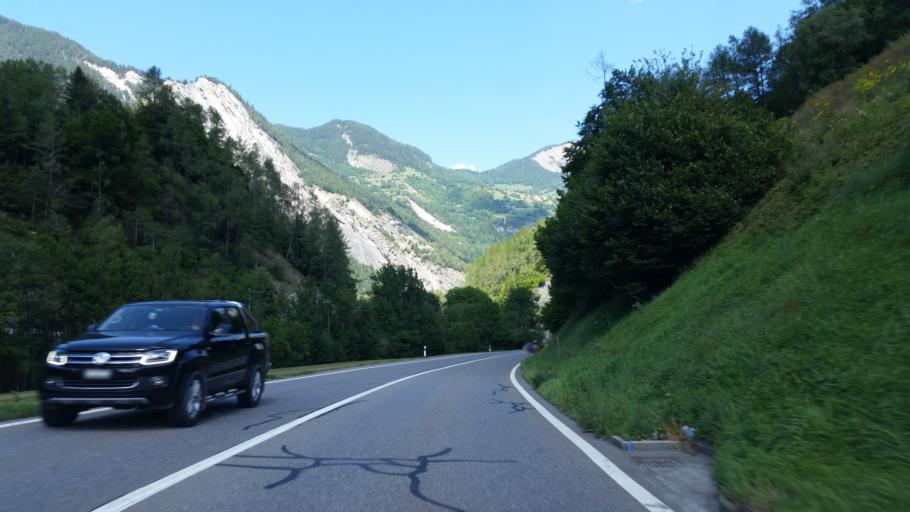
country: CH
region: Valais
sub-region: Entremont District
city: Orsieres
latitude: 46.0698
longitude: 7.1538
